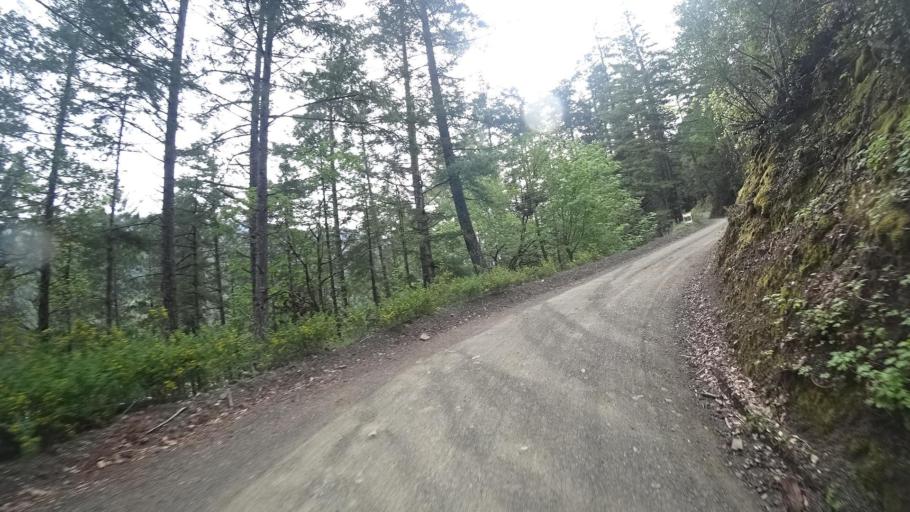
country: US
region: California
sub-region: Humboldt County
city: Redway
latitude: 40.3210
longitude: -123.8336
